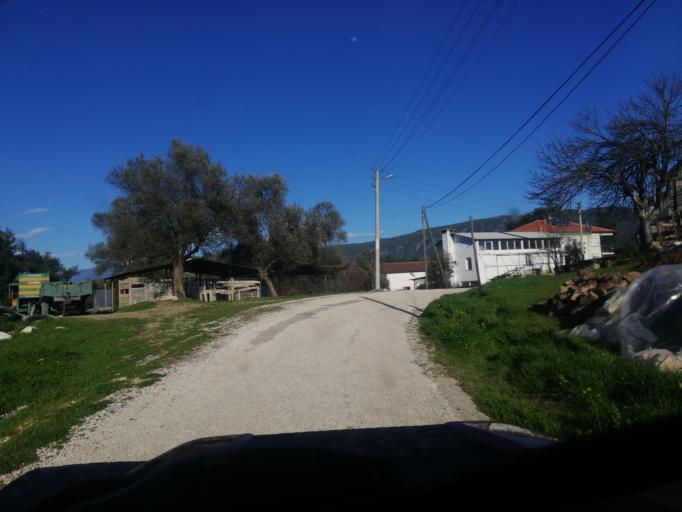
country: TR
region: Antalya
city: Kas
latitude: 36.2899
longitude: 29.7108
